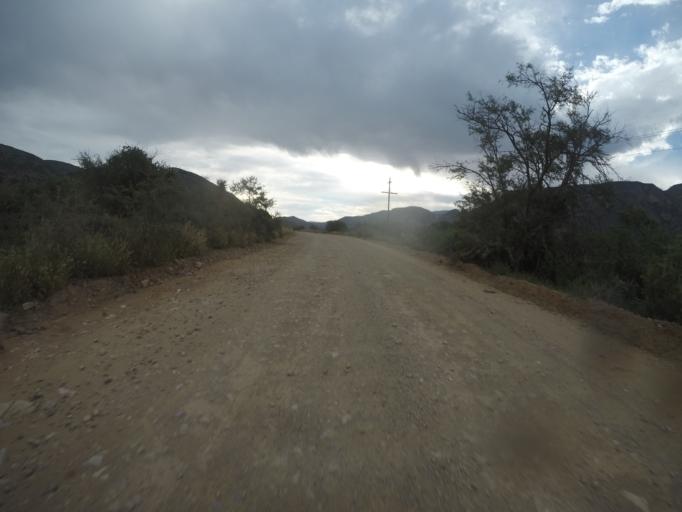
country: ZA
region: Eastern Cape
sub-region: Cacadu District Municipality
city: Willowmore
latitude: -33.5269
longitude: 23.8583
